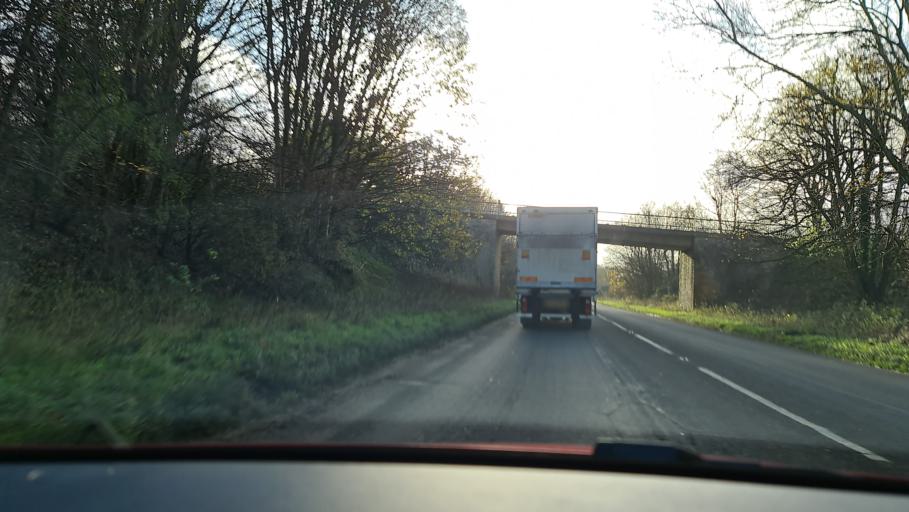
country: GB
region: England
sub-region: Buckinghamshire
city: Great Missenden
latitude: 51.7014
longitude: -0.7004
